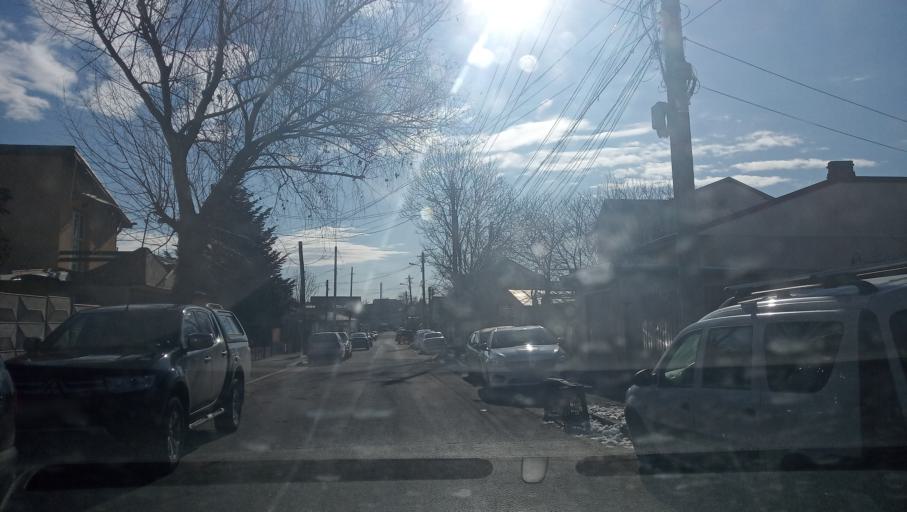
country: RO
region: Ilfov
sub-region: Comuna Fundeni-Dobroesti
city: Fundeni
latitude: 44.4621
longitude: 26.1381
